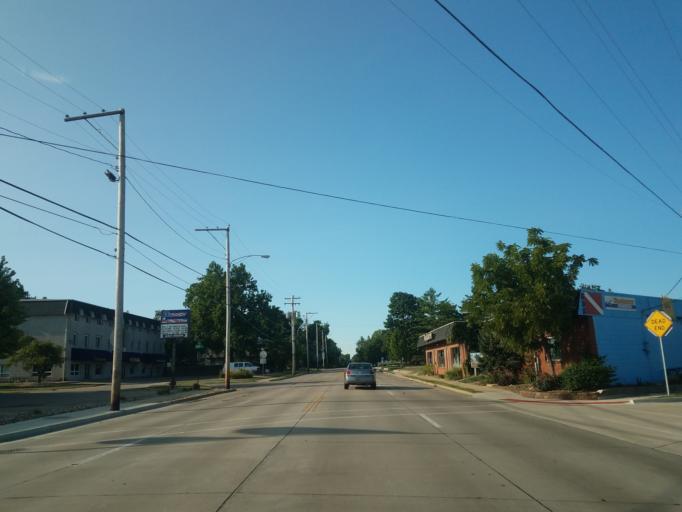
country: US
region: Illinois
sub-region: McLean County
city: Normal
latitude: 40.5090
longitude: -88.9824
